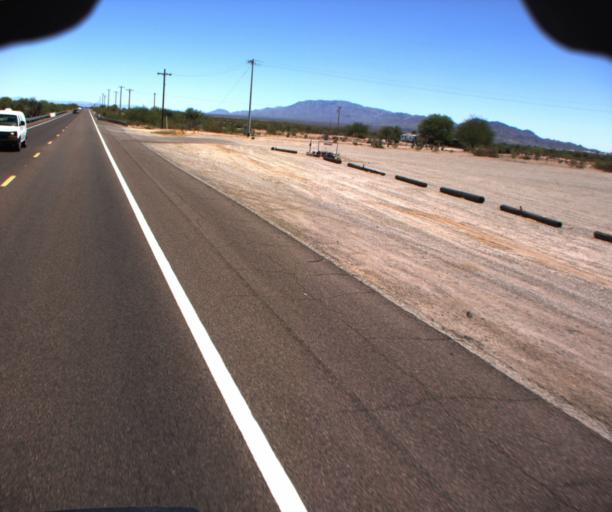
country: US
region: Arizona
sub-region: La Paz County
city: Salome
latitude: 33.7643
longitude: -113.6462
